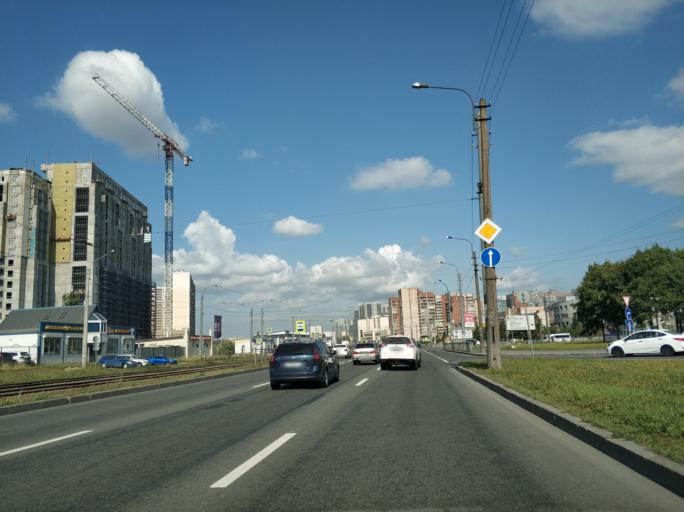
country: RU
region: St.-Petersburg
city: Obukhovo
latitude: 59.8999
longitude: 30.4594
